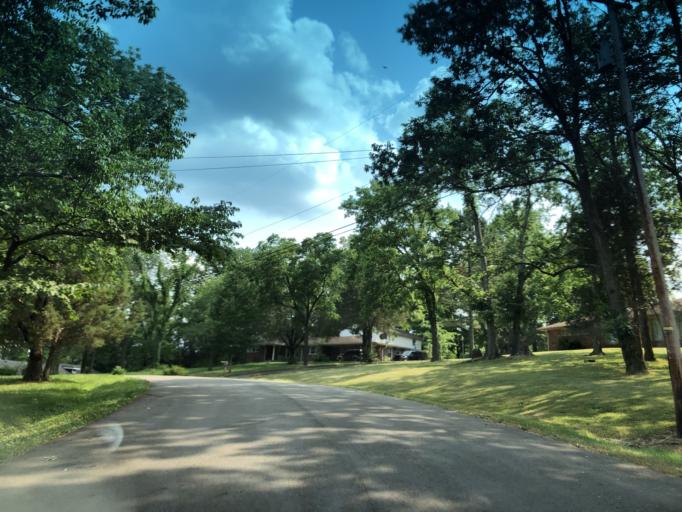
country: US
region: Tennessee
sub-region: Davidson County
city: Goodlettsville
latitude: 36.2692
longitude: -86.7314
